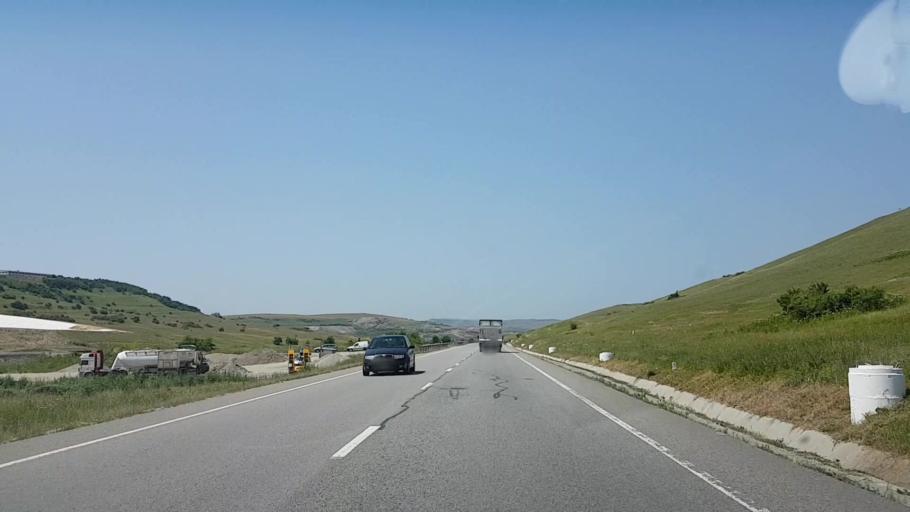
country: RO
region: Cluj
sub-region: Comuna Apahida
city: Dezmir
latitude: 46.7489
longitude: 23.7071
